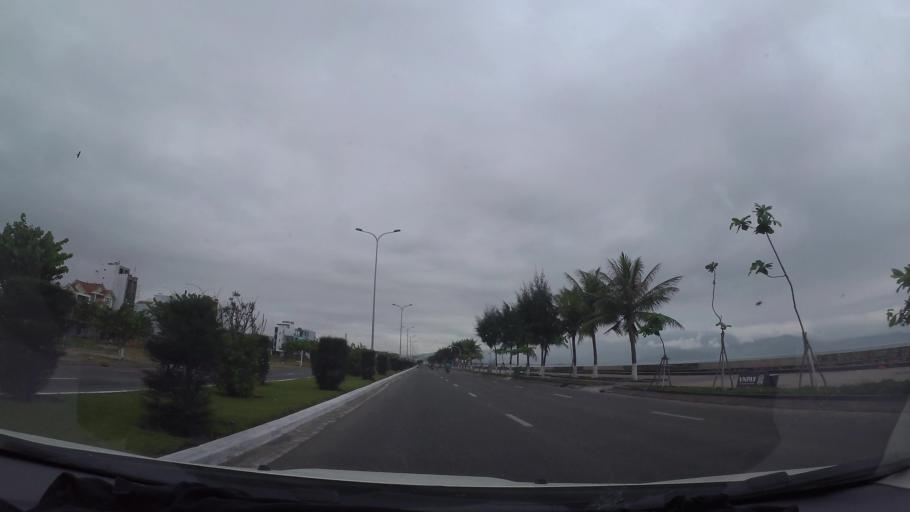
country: VN
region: Da Nang
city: Lien Chieu
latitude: 16.0821
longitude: 108.1653
